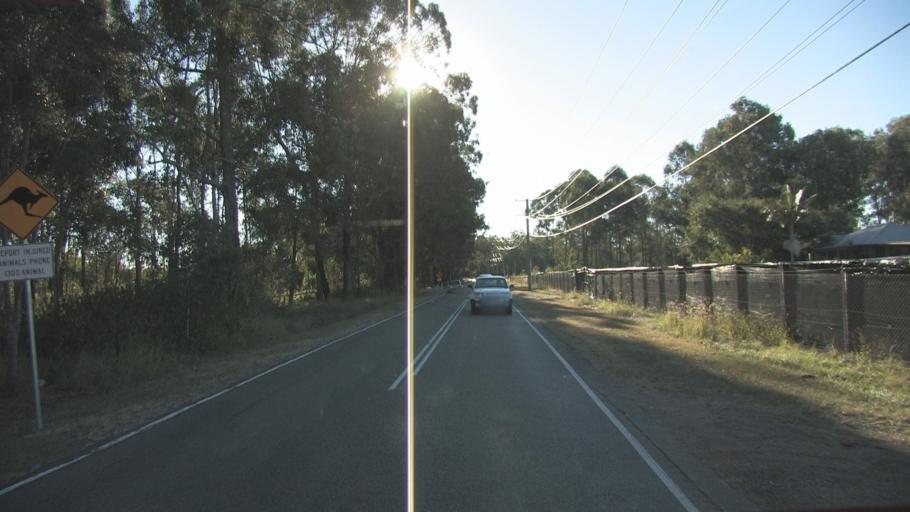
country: AU
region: Queensland
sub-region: Logan
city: Chambers Flat
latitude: -27.7488
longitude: 153.0761
